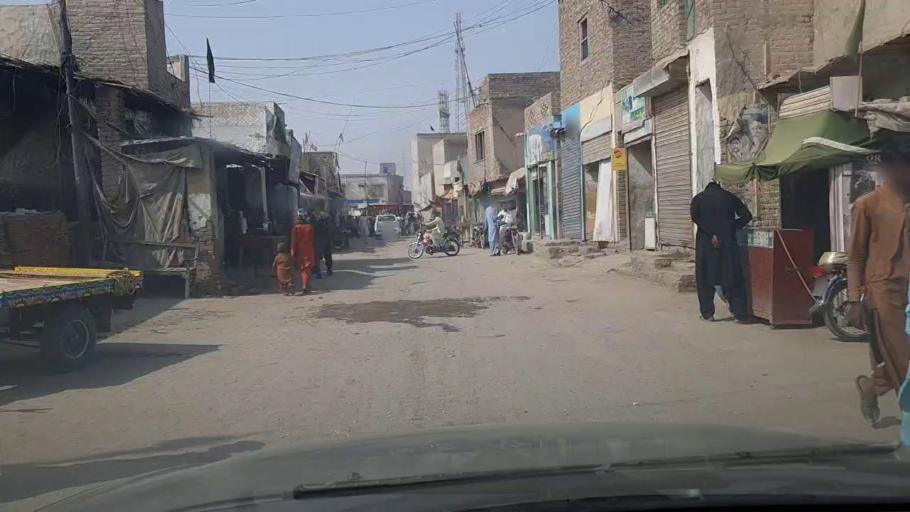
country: PK
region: Sindh
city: Mirpur Mathelo
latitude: 27.9161
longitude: 69.5213
